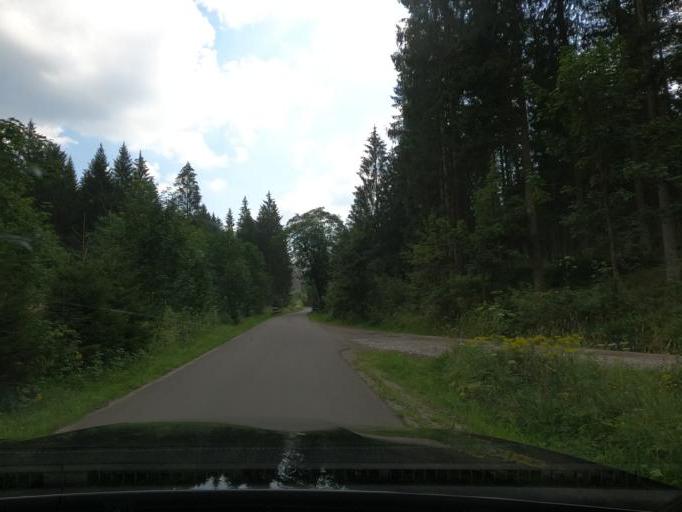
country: DE
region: Lower Saxony
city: Clausthal-Zellerfeld
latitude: 51.7828
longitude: 10.3002
